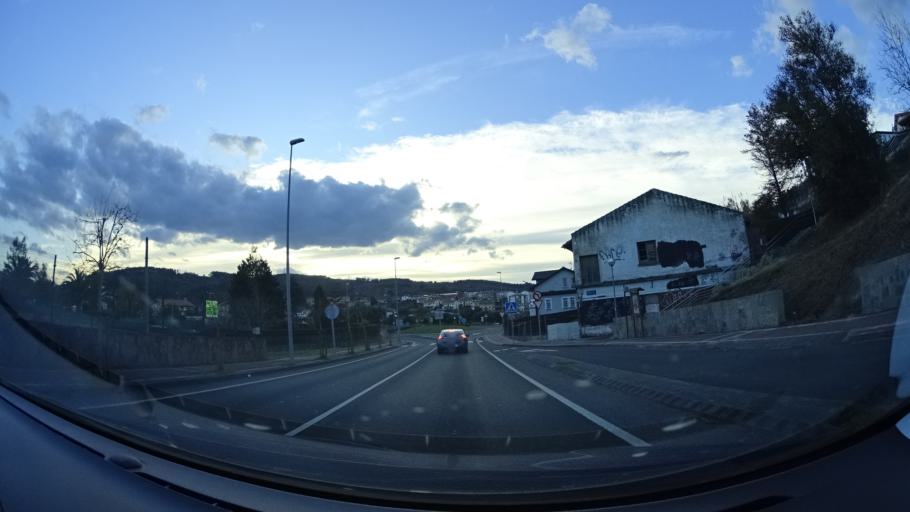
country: ES
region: Basque Country
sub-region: Bizkaia
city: Plentzia
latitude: 43.4022
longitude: -2.9415
